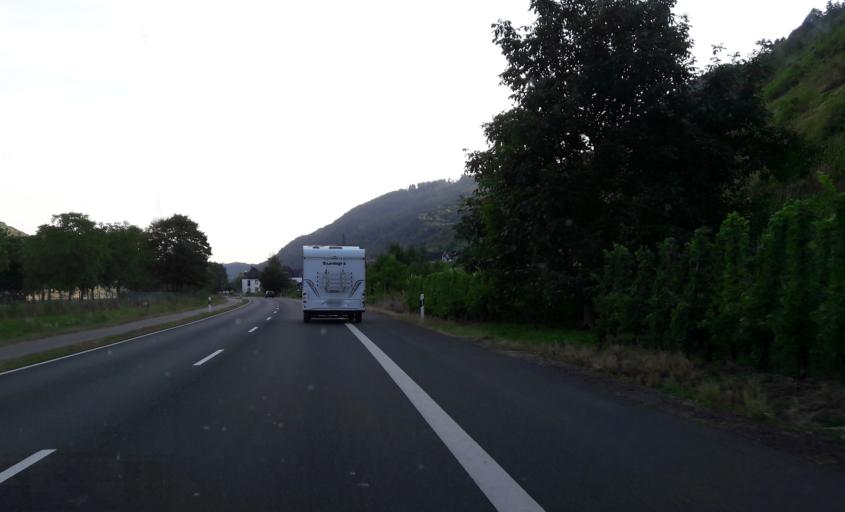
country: DE
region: Rheinland-Pfalz
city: Sankt Aldegund
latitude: 50.0876
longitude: 7.1325
